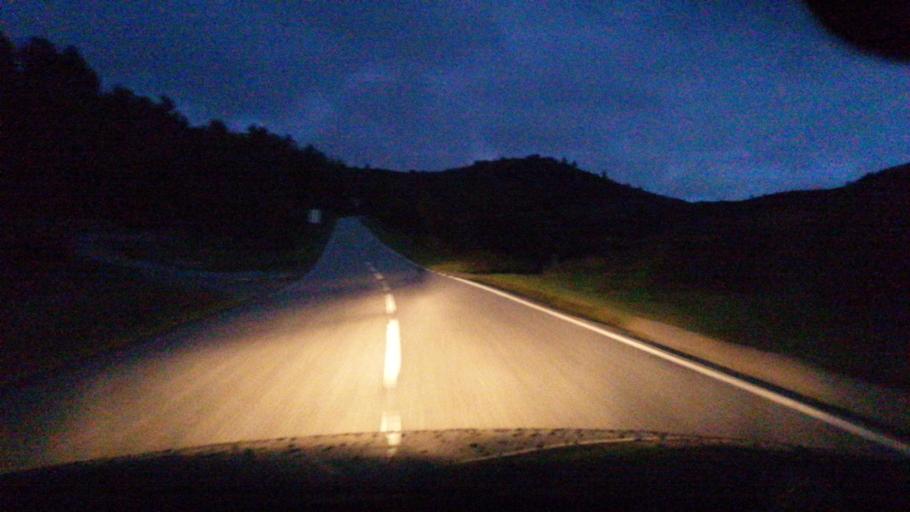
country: PT
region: Viseu
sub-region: Tabuaco
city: Tabuaco
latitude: 41.1426
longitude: -7.5327
